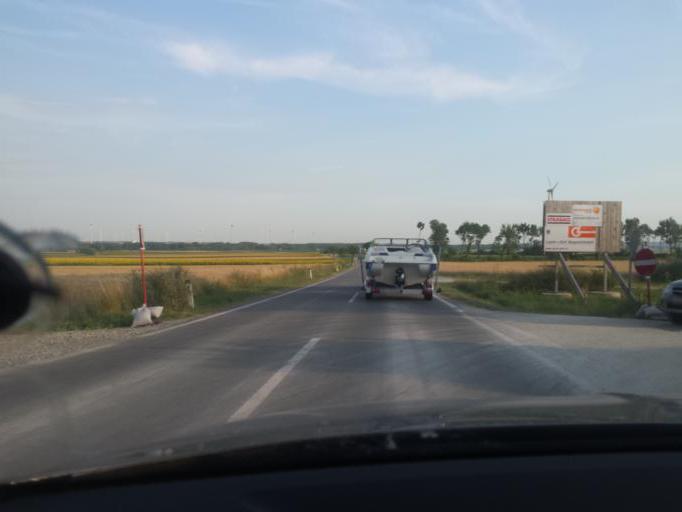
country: AT
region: Lower Austria
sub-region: Politischer Bezirk Bruck an der Leitha
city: Petronell-Carnuntum
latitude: 48.0943
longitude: 16.8620
